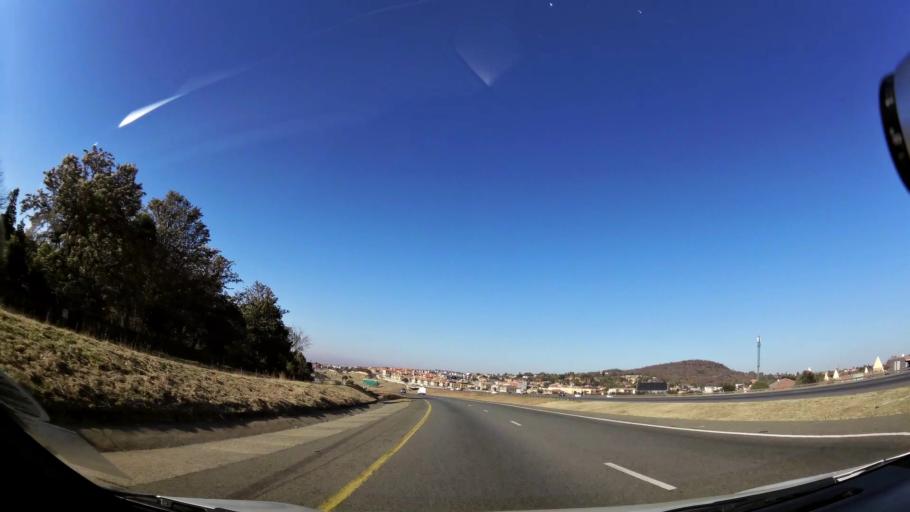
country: ZA
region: Gauteng
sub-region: Ekurhuleni Metropolitan Municipality
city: Germiston
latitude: -26.2837
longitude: 28.1017
